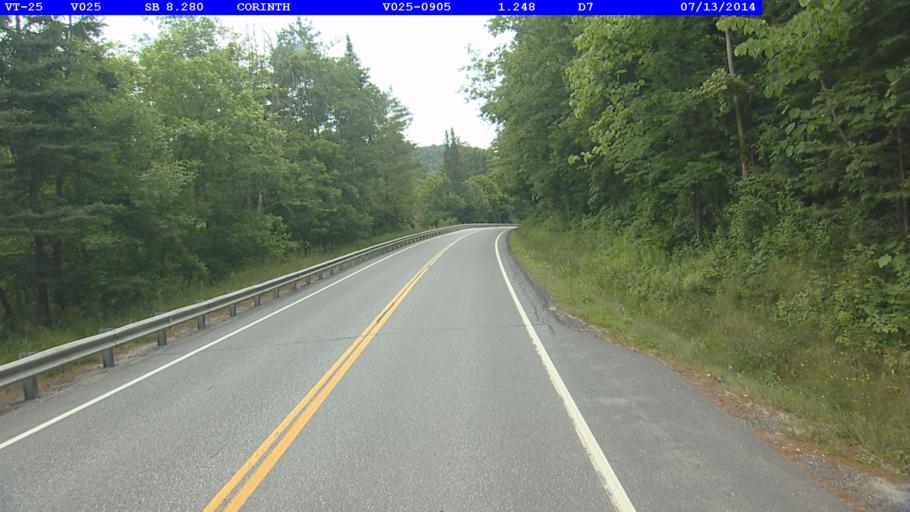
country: US
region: New Hampshire
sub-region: Grafton County
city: Haverhill
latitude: 44.0540
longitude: -72.2197
